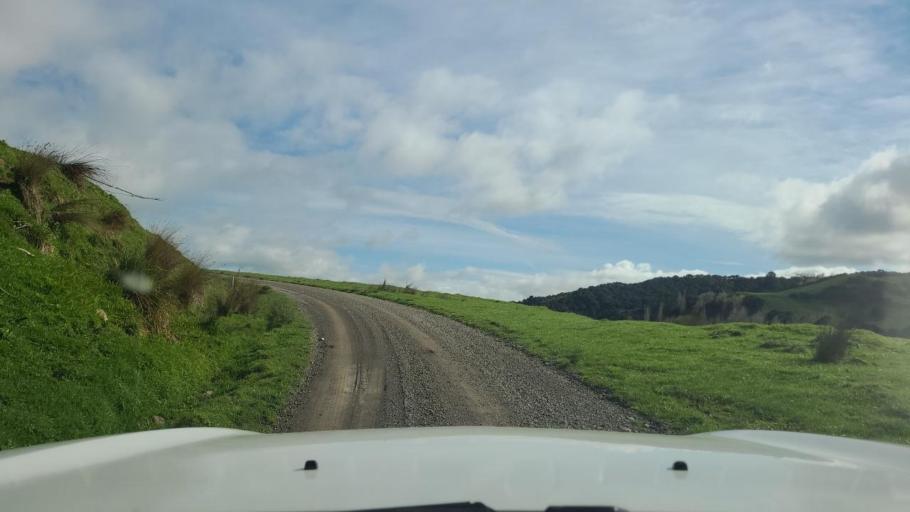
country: NZ
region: Wellington
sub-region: South Wairarapa District
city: Waipawa
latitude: -41.2647
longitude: 175.6855
